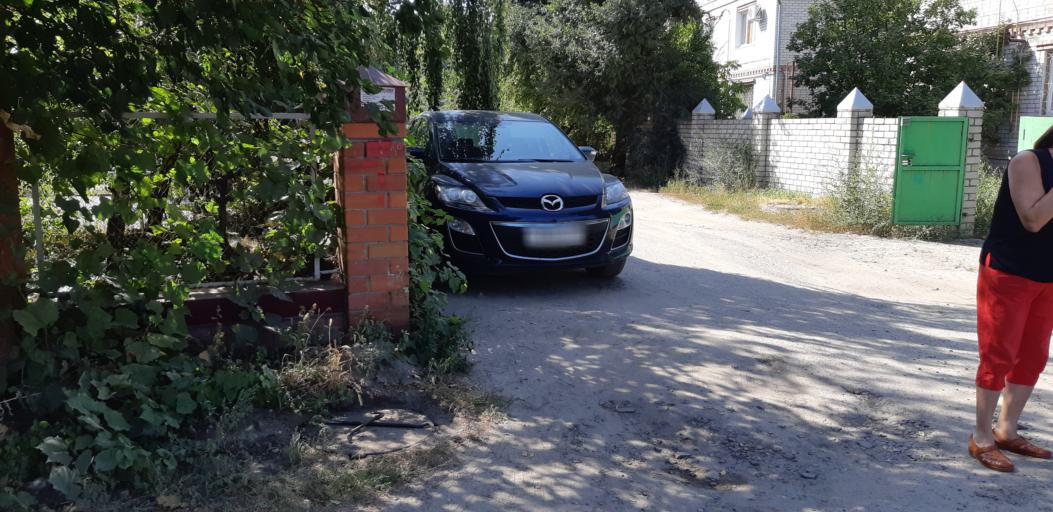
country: RU
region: Voronezj
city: Voronezh
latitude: 51.6644
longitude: 39.1688
